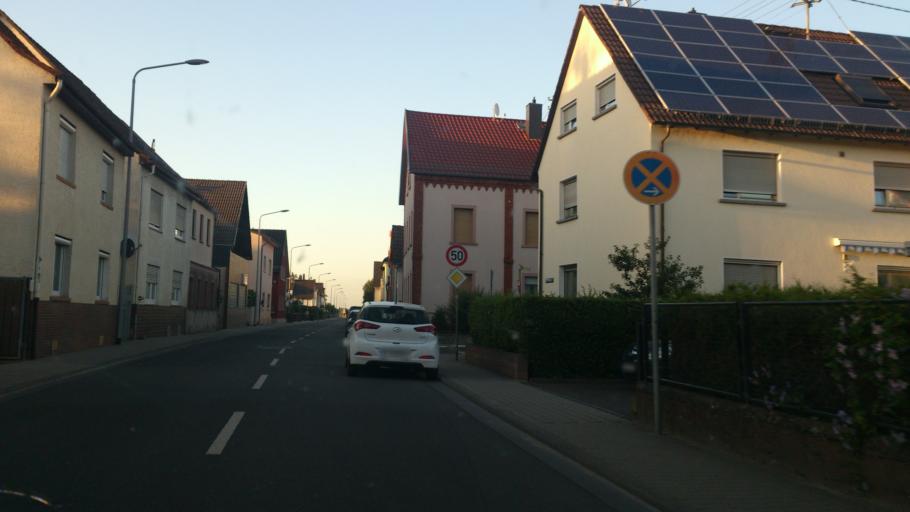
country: DE
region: Hesse
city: Raunheim
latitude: 50.0409
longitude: 8.4717
